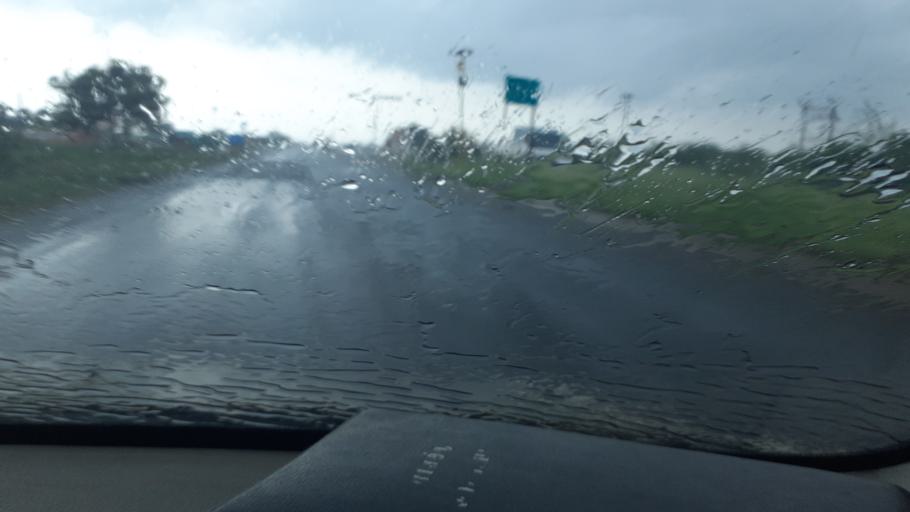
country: IN
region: Tamil Nadu
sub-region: Thoothukkudi
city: Kovilpatti
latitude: 9.0897
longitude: 77.8045
